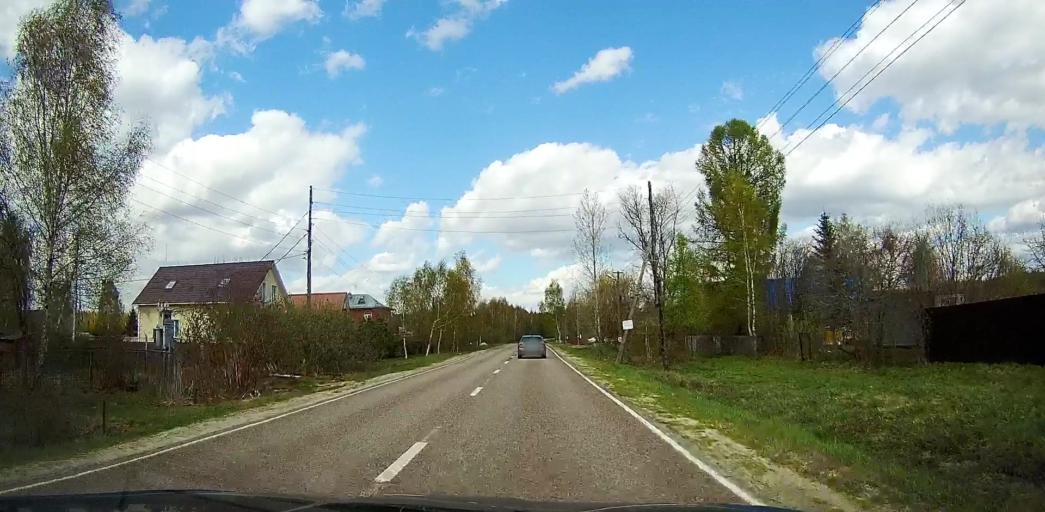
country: RU
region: Moskovskaya
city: Davydovo
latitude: 55.5878
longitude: 38.8299
